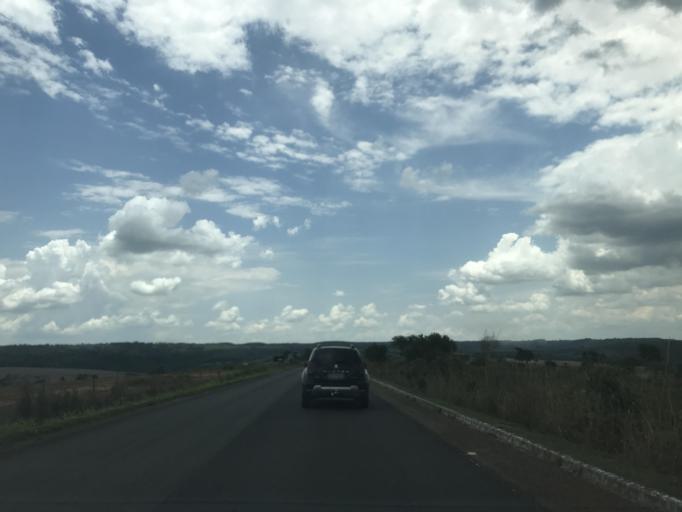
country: BR
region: Goias
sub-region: Vianopolis
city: Vianopolis
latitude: -16.9462
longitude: -48.5661
